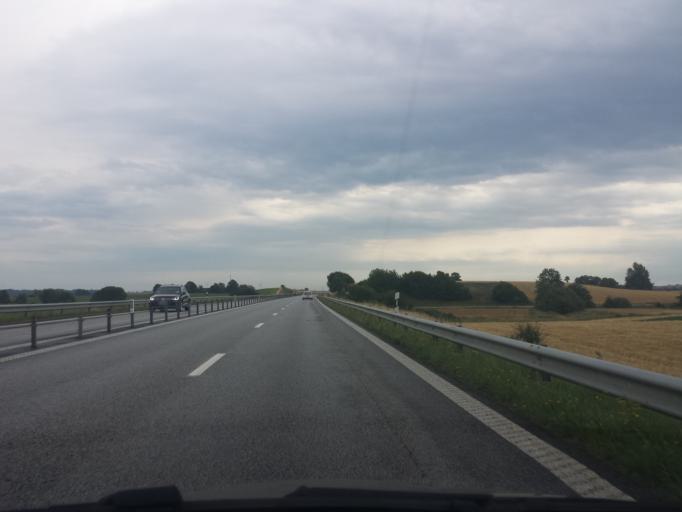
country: SE
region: Skane
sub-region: Skurups Kommun
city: Rydsgard
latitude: 55.4816
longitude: 13.6115
